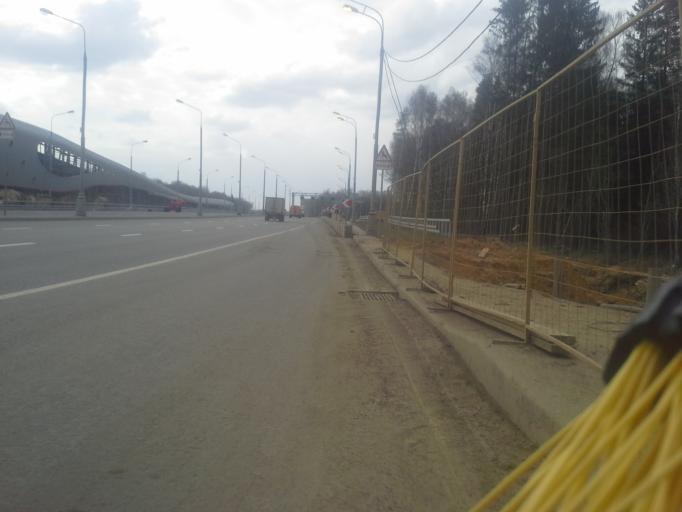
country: RU
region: Moscow
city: Solntsevo
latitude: 55.6020
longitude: 37.4078
